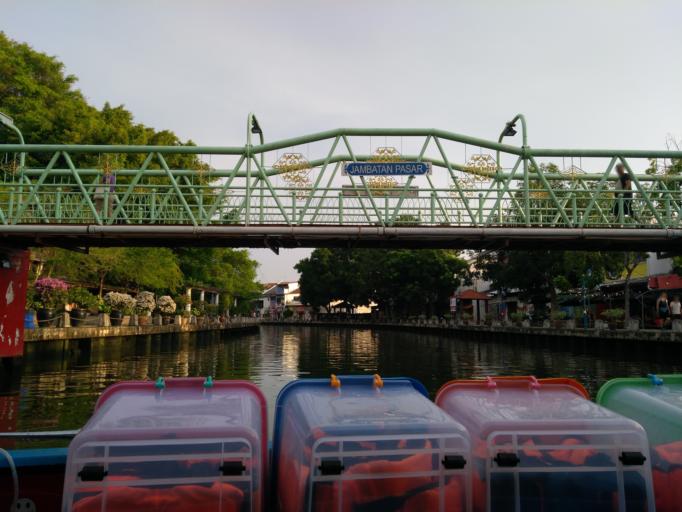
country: MY
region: Melaka
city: Malacca
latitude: 2.1990
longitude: 102.2485
